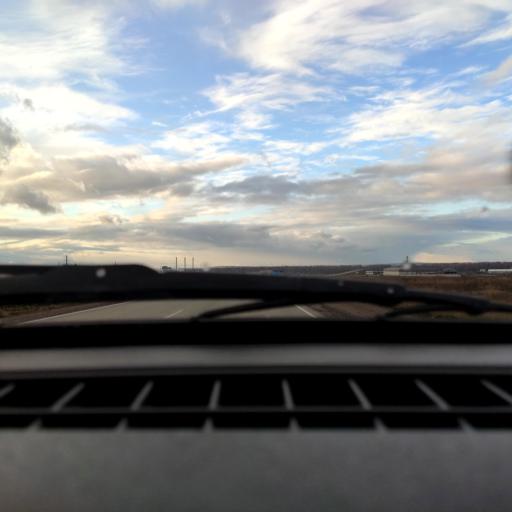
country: RU
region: Bashkortostan
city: Iglino
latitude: 54.7595
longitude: 56.2745
